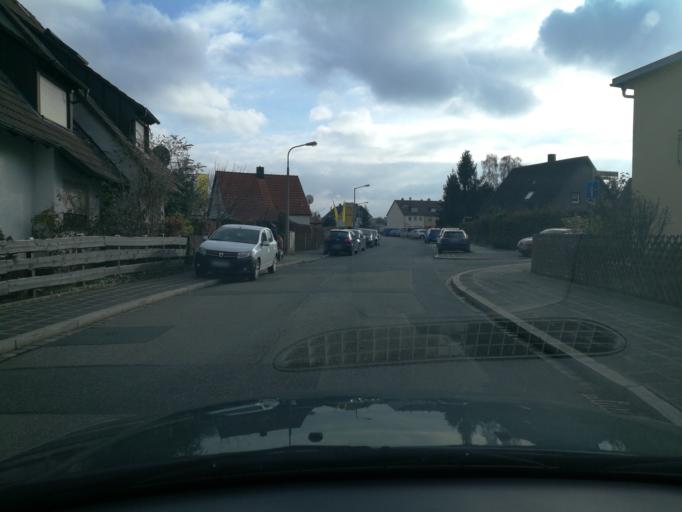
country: DE
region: Bavaria
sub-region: Regierungsbezirk Mittelfranken
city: Grossreuth bei Schweinau
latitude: 49.4537
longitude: 11.0261
